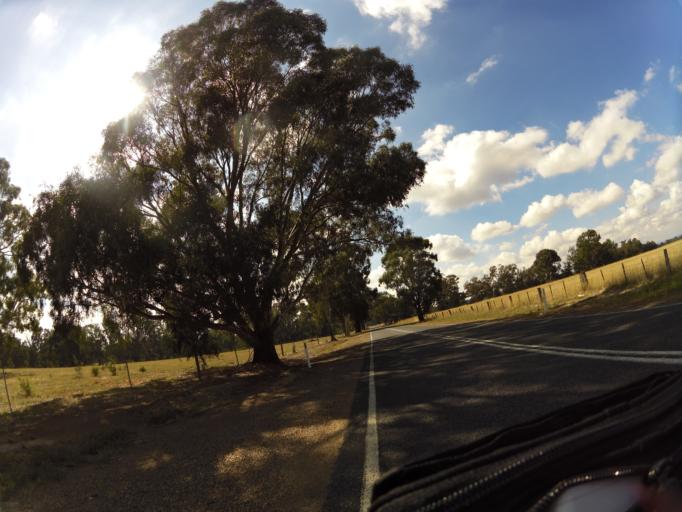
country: AU
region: Victoria
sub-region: Benalla
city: Benalla
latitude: -36.5797
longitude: 145.9941
